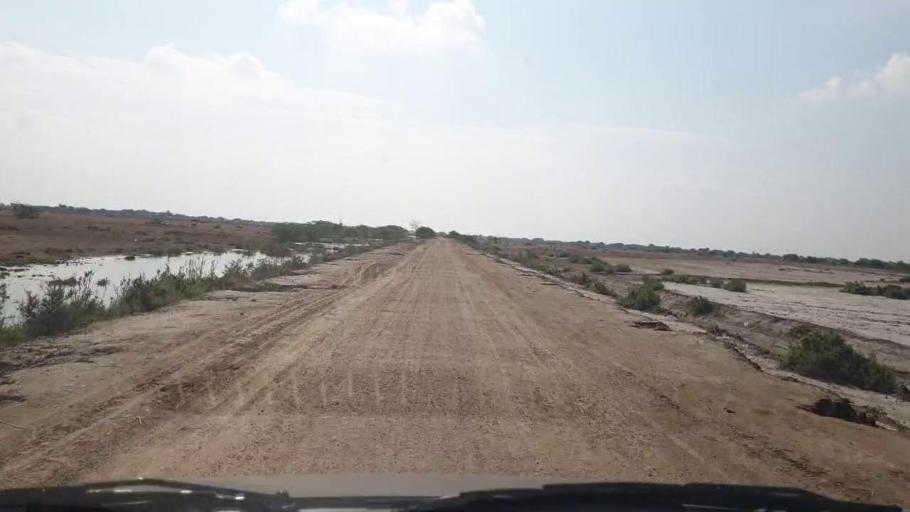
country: PK
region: Sindh
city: Badin
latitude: 24.4956
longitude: 68.6119
